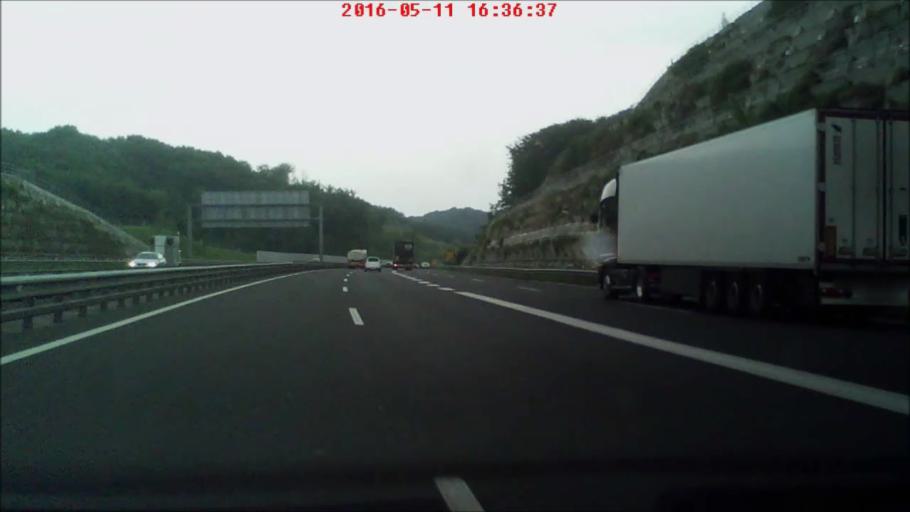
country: SI
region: Pesnica
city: Pesnica pri Mariboru
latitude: 46.5821
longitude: 15.6893
